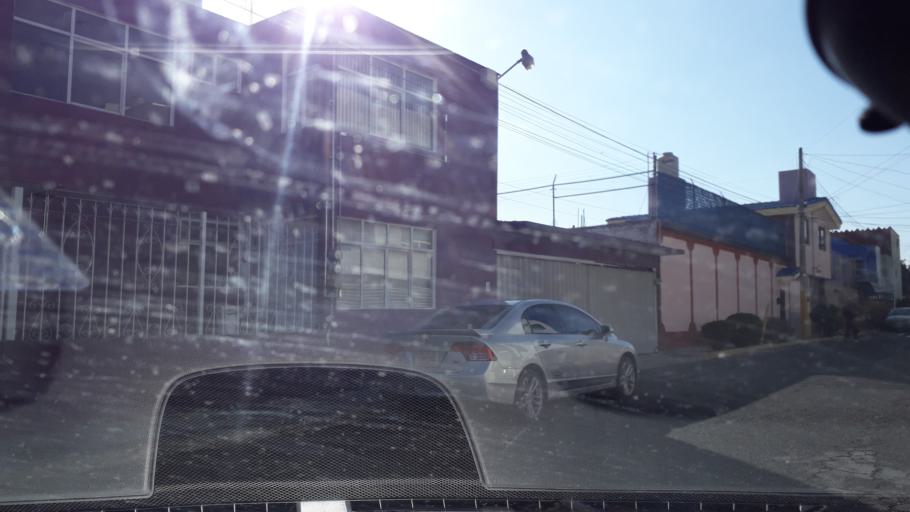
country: MX
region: Puebla
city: Puebla
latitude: 19.0635
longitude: -98.2187
